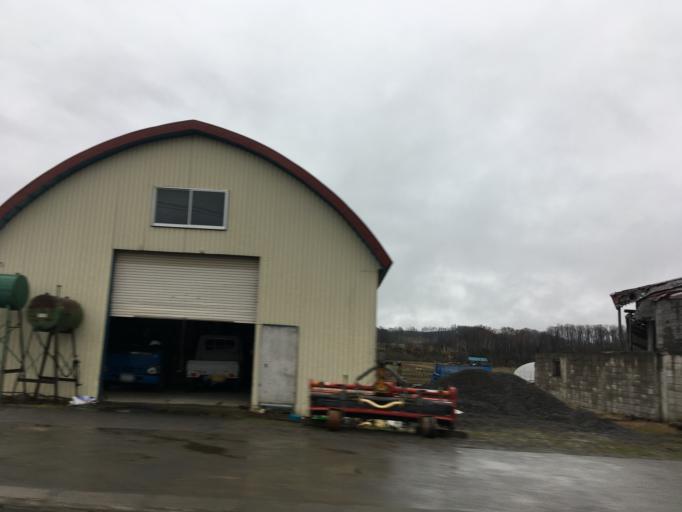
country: JP
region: Hokkaido
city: Nayoro
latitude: 44.0979
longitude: 142.4748
